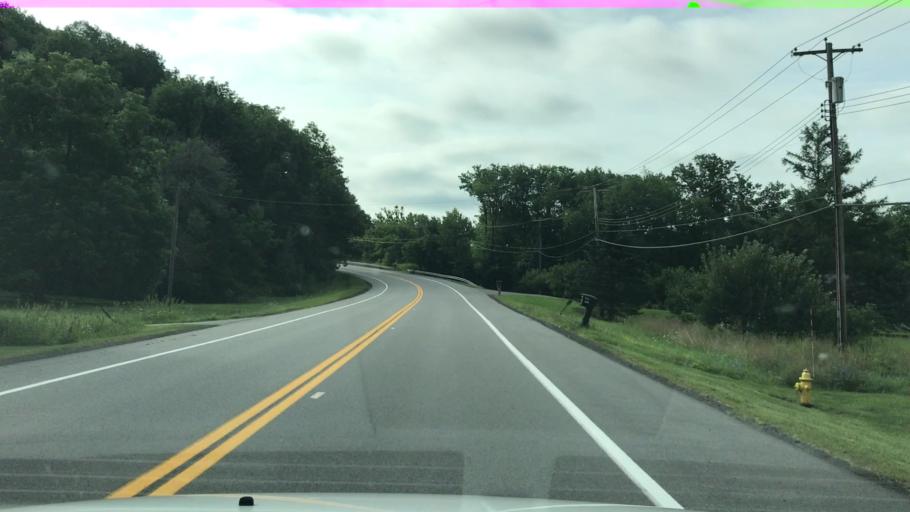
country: US
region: New York
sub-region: Erie County
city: Alden
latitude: 42.8518
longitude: -78.4922
